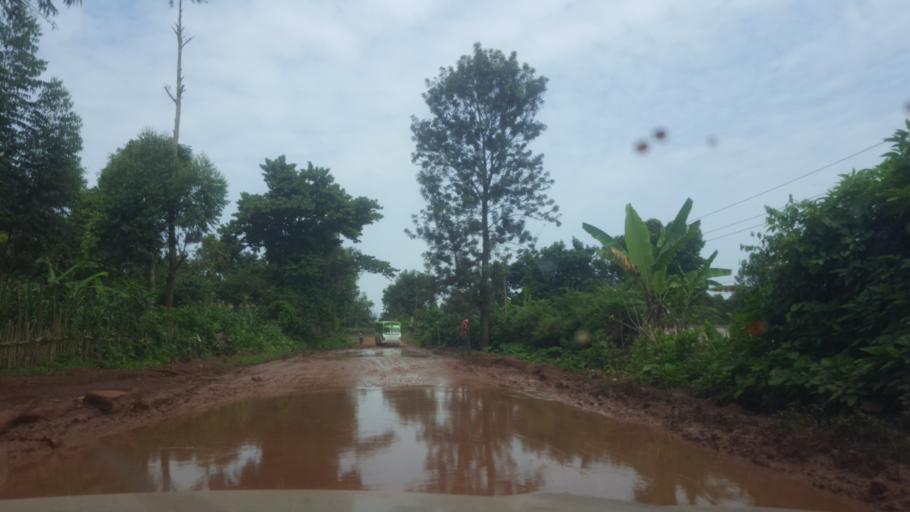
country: ET
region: Southern Nations, Nationalities, and People's Region
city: Tippi
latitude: 7.2427
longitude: 35.3358
